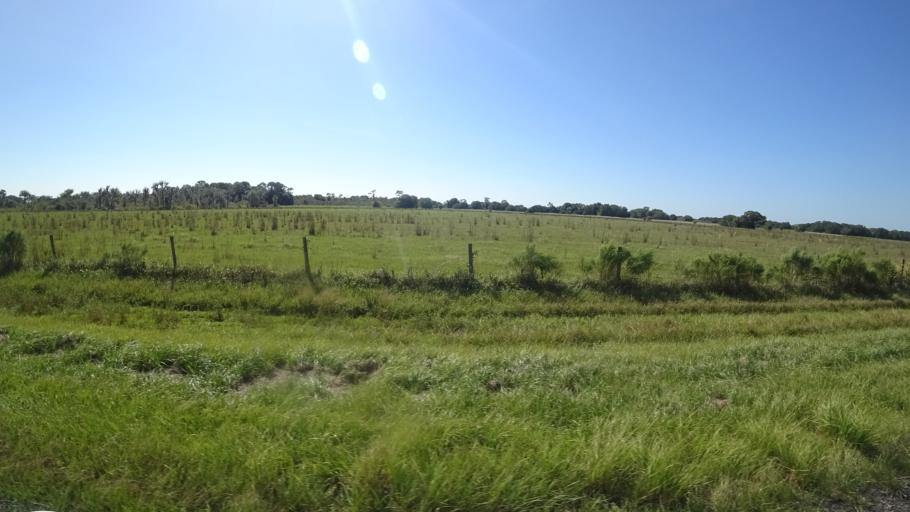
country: US
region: Florida
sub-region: Sarasota County
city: Warm Mineral Springs
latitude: 27.2737
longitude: -82.1730
